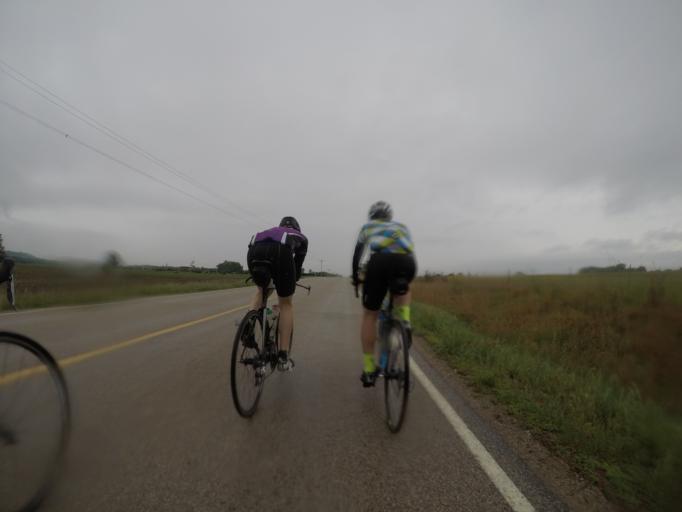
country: US
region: Kansas
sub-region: Pottawatomie County
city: Wamego
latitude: 39.3556
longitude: -96.2212
